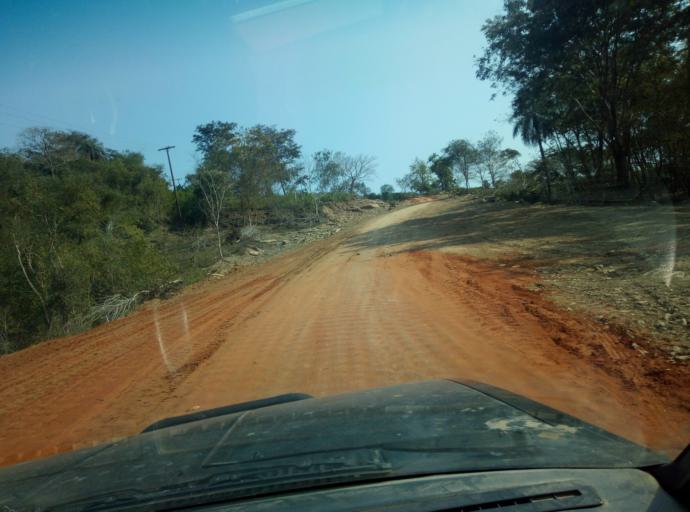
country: PY
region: Caaguazu
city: Coronel Oviedo
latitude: -25.3298
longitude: -56.3220
